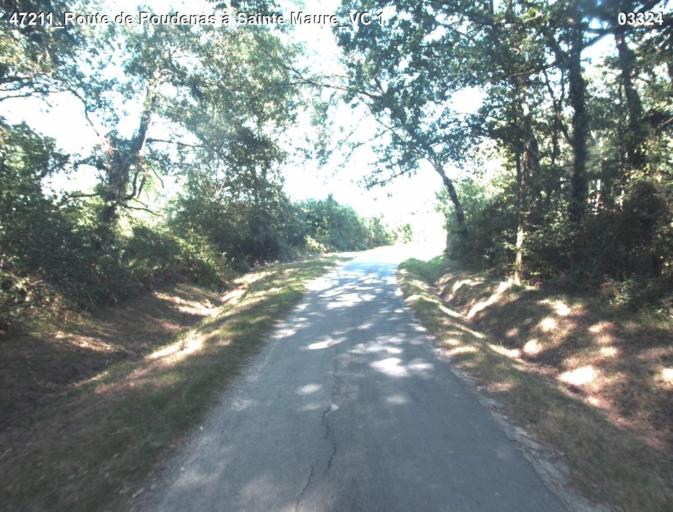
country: FR
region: Aquitaine
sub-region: Departement du Lot-et-Garonne
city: Mezin
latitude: 44.0221
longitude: 0.1983
